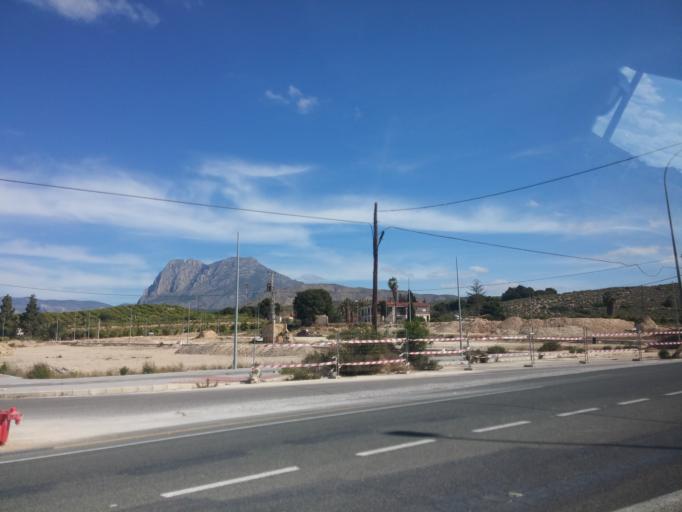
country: ES
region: Valencia
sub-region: Provincia de Alicante
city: Villajoyosa
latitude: 38.5234
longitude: -0.1954
